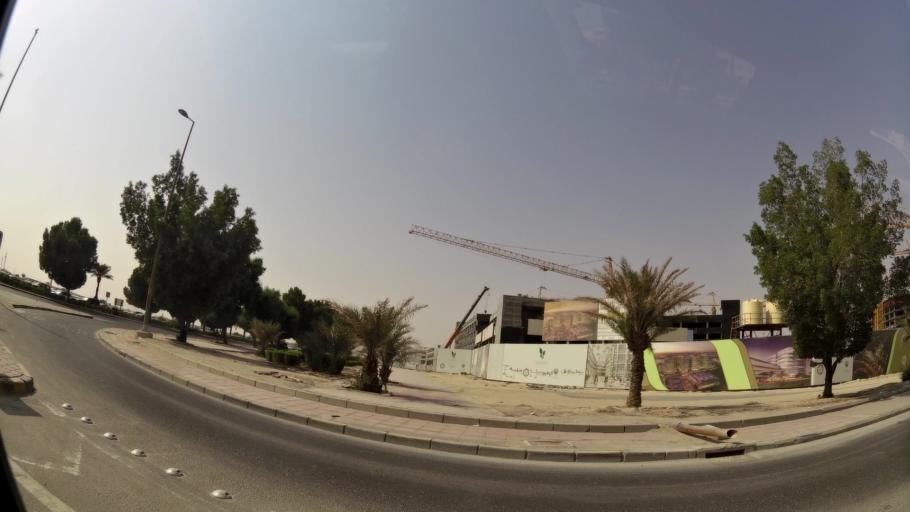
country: KW
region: Muhafazat al Jahra'
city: Al Jahra'
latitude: 29.3349
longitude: 47.6834
